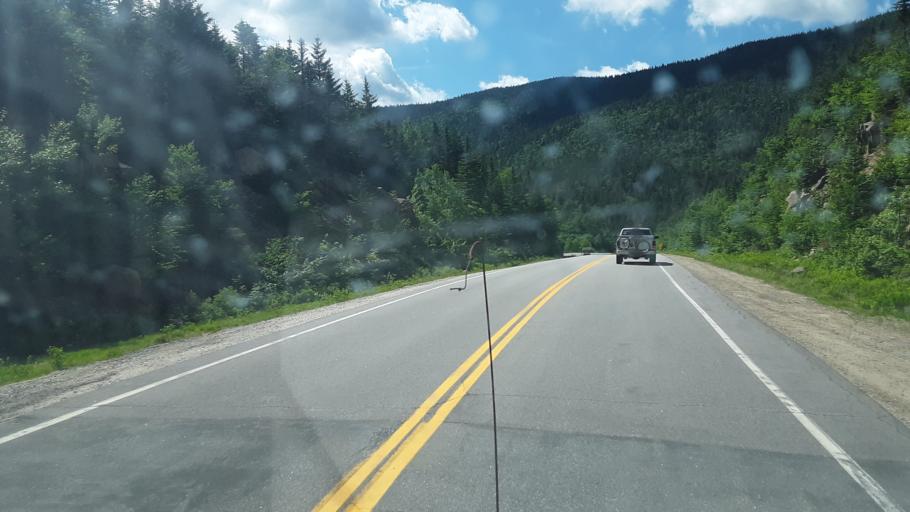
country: US
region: New Hampshire
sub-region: Grafton County
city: Woodstock
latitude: 44.0252
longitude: -71.4931
